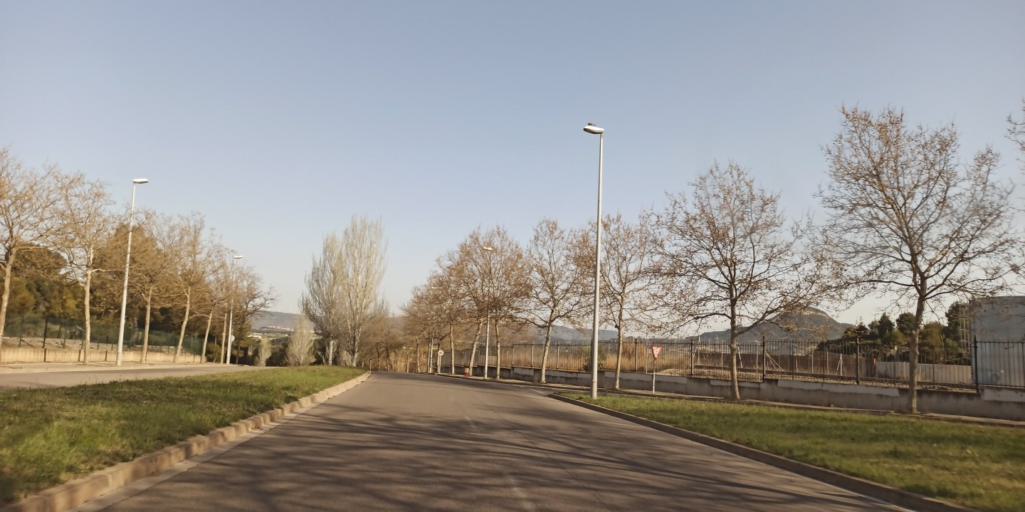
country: ES
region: Catalonia
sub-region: Provincia de Barcelona
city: La Pobla de Claramunt
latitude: 41.5722
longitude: 1.6679
